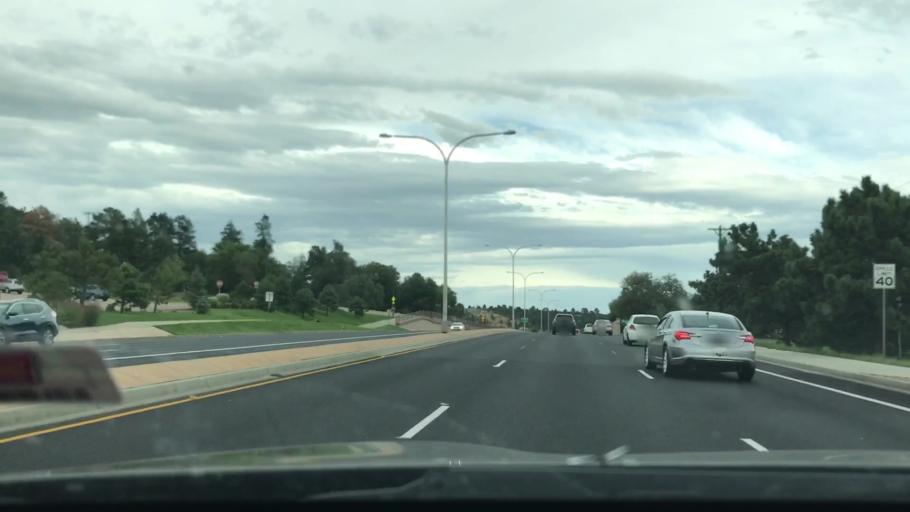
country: US
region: Colorado
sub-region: El Paso County
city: Colorado Springs
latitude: 38.8900
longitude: -104.7970
